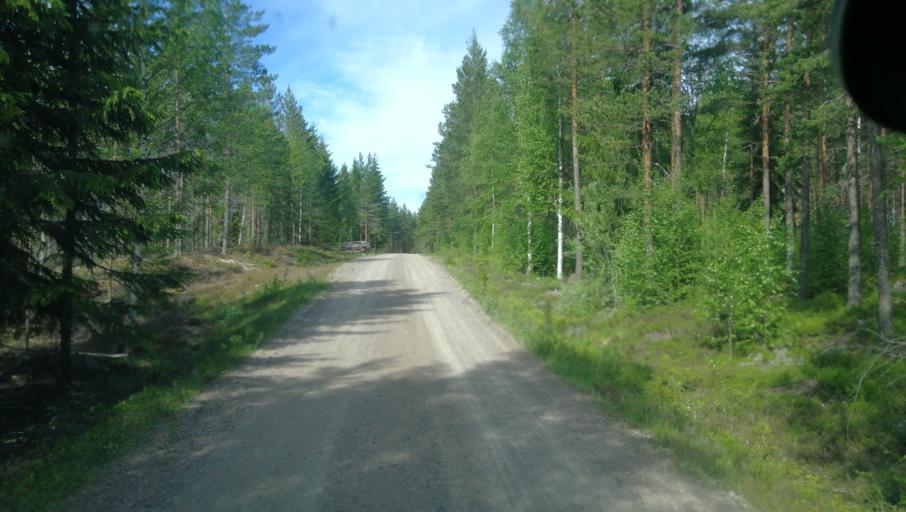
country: SE
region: Dalarna
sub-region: Vansbro Kommun
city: Vansbro
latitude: 60.8192
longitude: 14.1799
